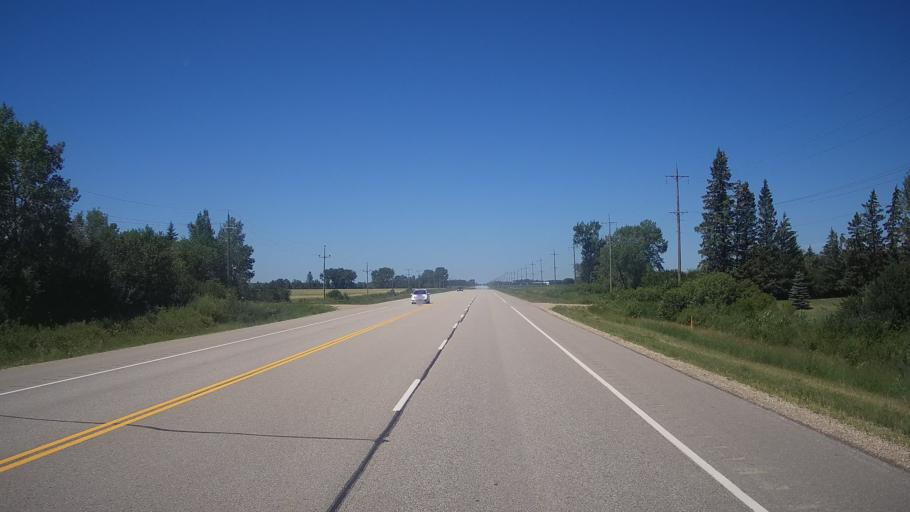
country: CA
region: Manitoba
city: Neepawa
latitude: 50.2250
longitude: -99.2822
